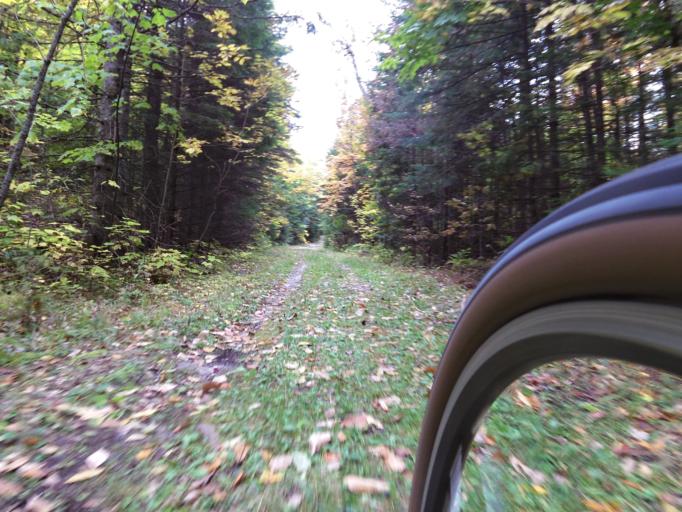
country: CA
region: Quebec
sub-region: Outaouais
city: Wakefield
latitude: 45.5949
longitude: -76.0679
